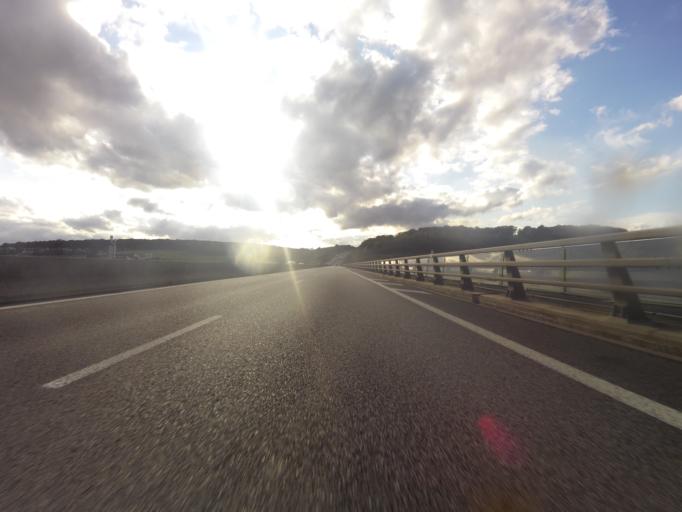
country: FR
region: Haute-Normandie
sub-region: Departement de la Seine-Maritime
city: Aumale
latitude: 49.7832
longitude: 1.7553
